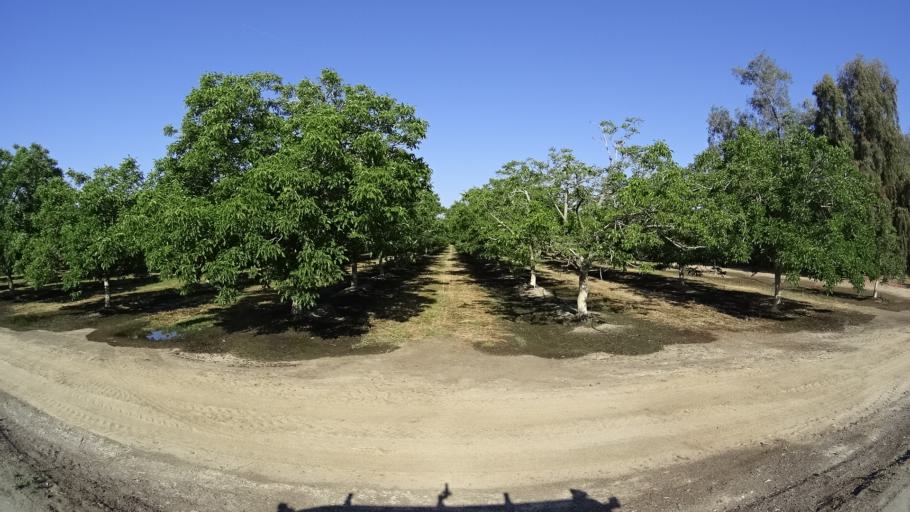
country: US
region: California
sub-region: Fresno County
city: Laton
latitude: 36.3968
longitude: -119.7180
